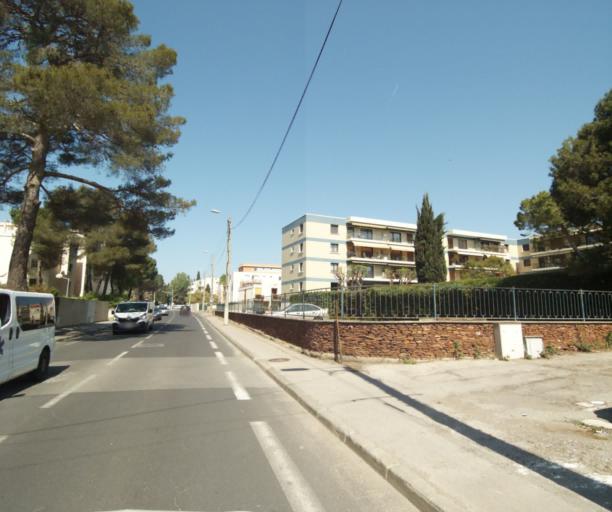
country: FR
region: Languedoc-Roussillon
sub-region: Departement de l'Herault
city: Montpellier
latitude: 43.6237
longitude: 3.8538
